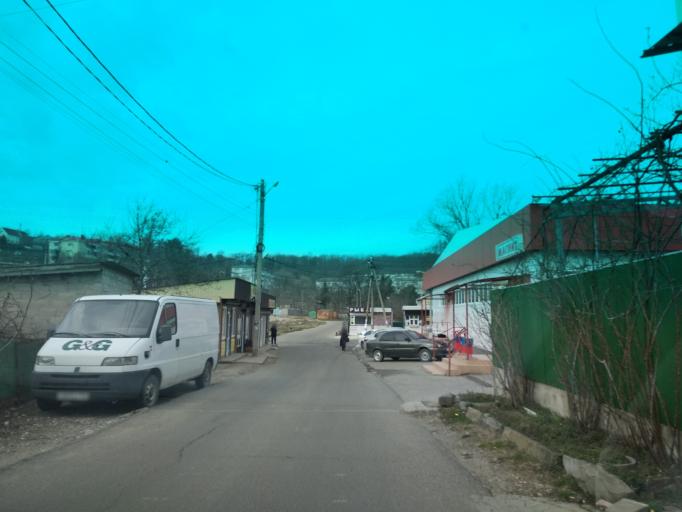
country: RU
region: Krasnodarskiy
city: Novomikhaylovskiy
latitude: 44.2518
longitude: 38.8352
